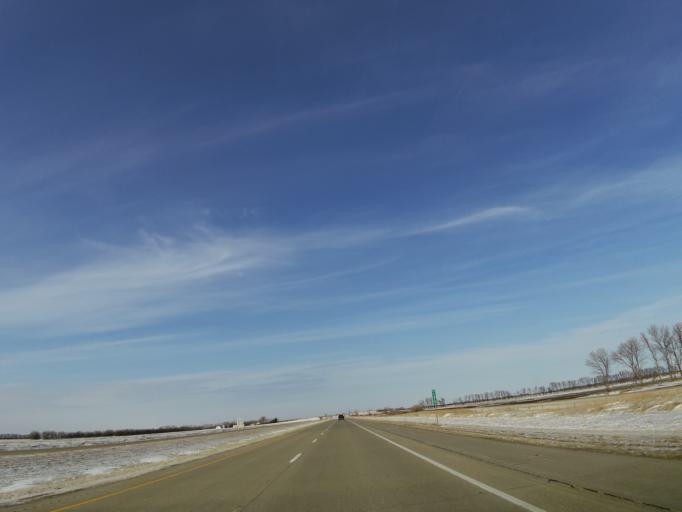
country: US
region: North Dakota
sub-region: Walsh County
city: Grafton
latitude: 48.4290
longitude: -97.1904
